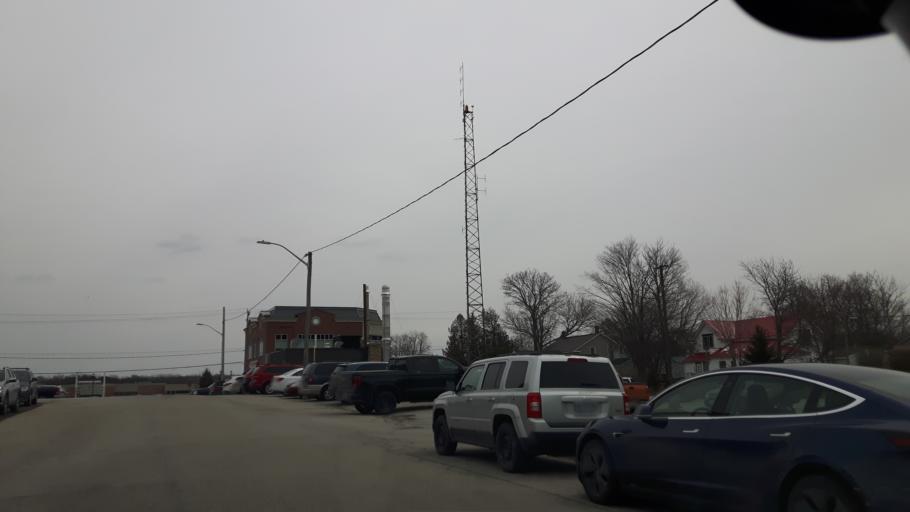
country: CA
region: Ontario
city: Goderich
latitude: 43.7496
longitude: -81.7062
